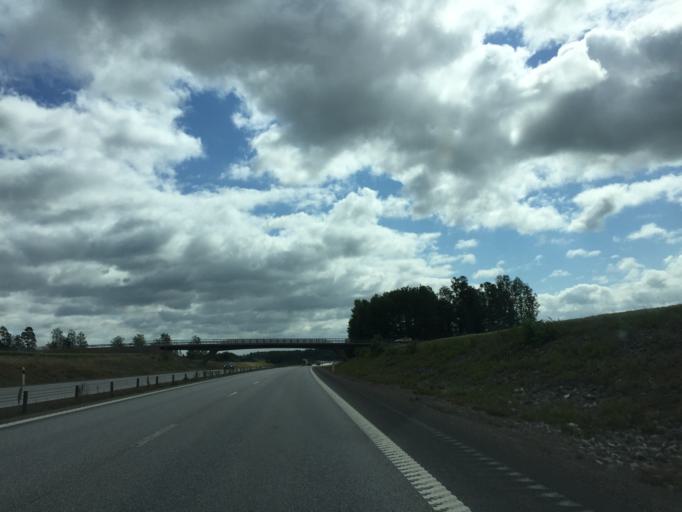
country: SE
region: OErebro
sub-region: Orebro Kommun
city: Vintrosa
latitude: 59.2452
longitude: 14.9951
